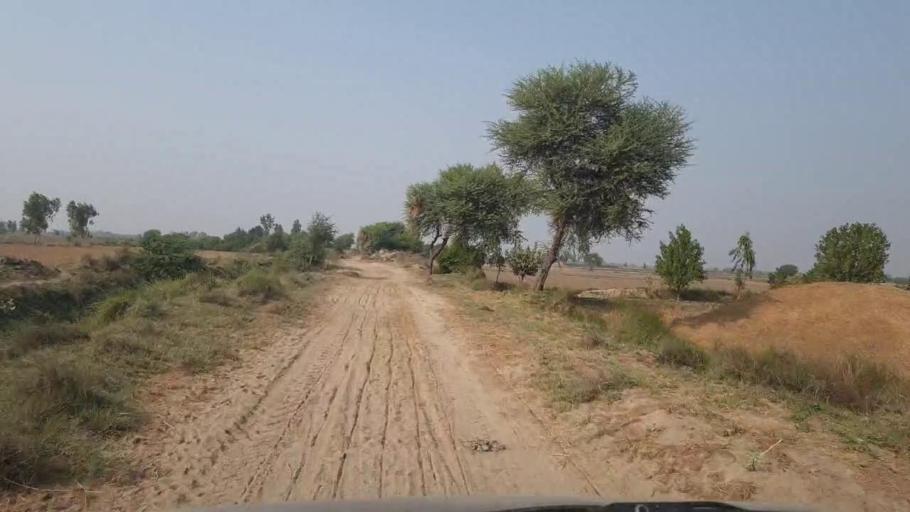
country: PK
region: Sindh
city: Tando Muhammad Khan
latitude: 25.0744
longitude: 68.3546
